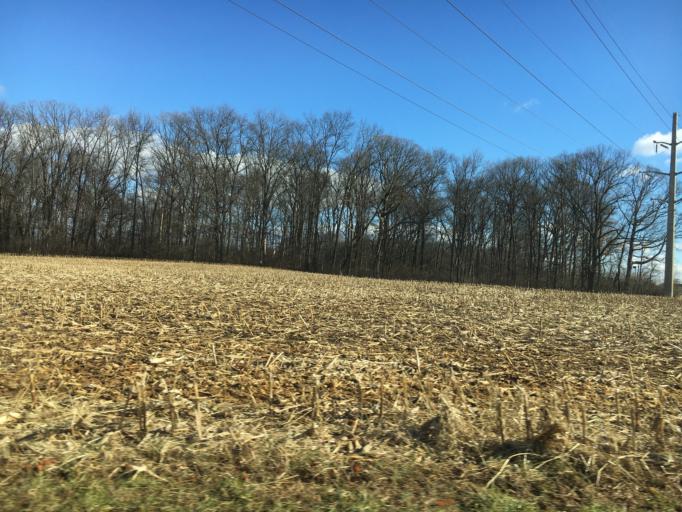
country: US
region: Pennsylvania
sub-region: Lehigh County
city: Stiles
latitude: 40.6424
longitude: -75.5134
